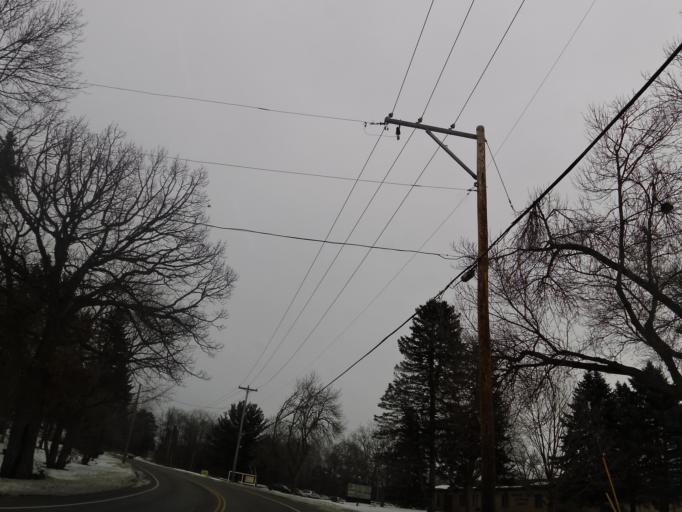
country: US
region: Minnesota
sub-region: Ramsey County
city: Maplewood
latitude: 44.9685
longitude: -93.0049
